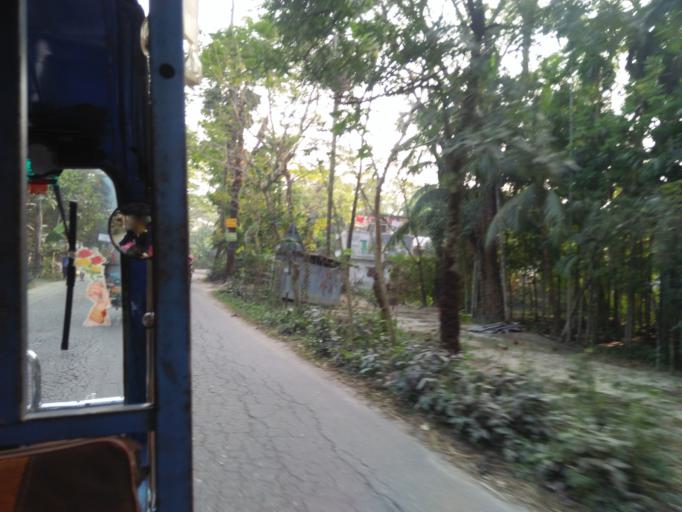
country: BD
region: Barisal
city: Bhola
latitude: 22.7034
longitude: 90.6412
